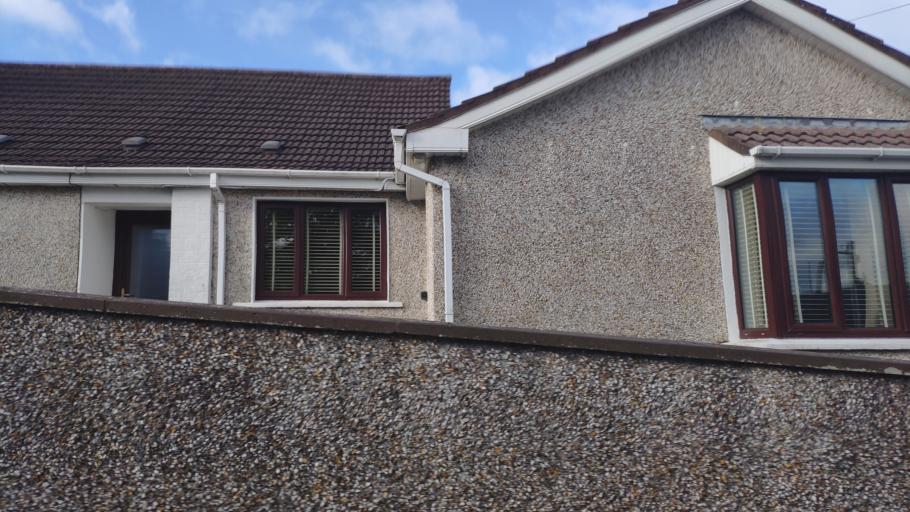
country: IE
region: Munster
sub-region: County Cork
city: Cork
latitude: 51.9111
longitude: -8.4831
